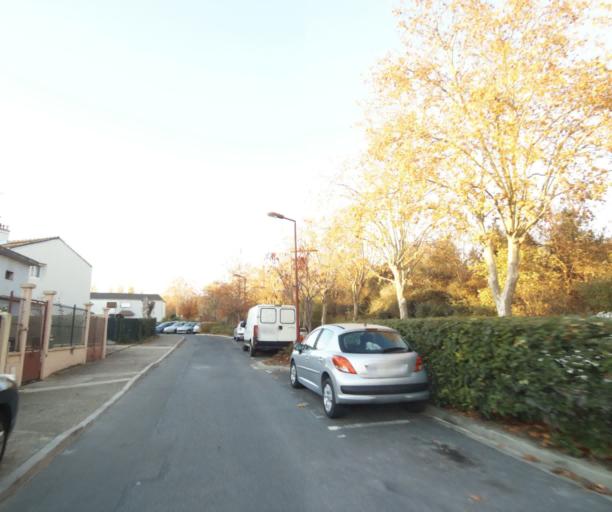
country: FR
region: Ile-de-France
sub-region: Departement du Val-d'Oise
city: Gonesse
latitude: 48.9881
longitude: 2.4360
